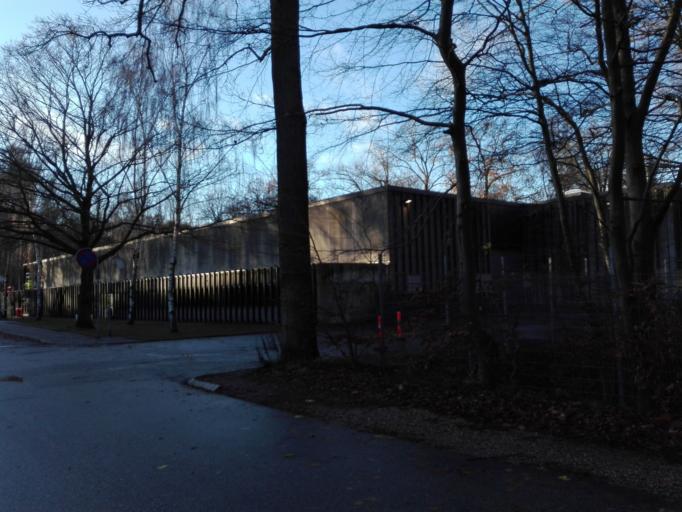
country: DK
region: Central Jutland
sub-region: Arhus Kommune
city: Arhus
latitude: 56.1348
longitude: 10.1983
